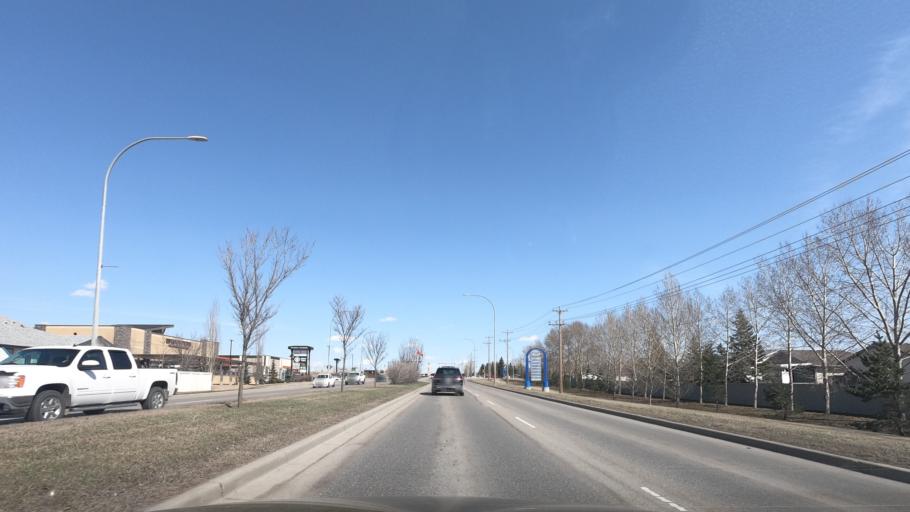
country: CA
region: Alberta
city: Airdrie
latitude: 51.3000
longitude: -114.0159
